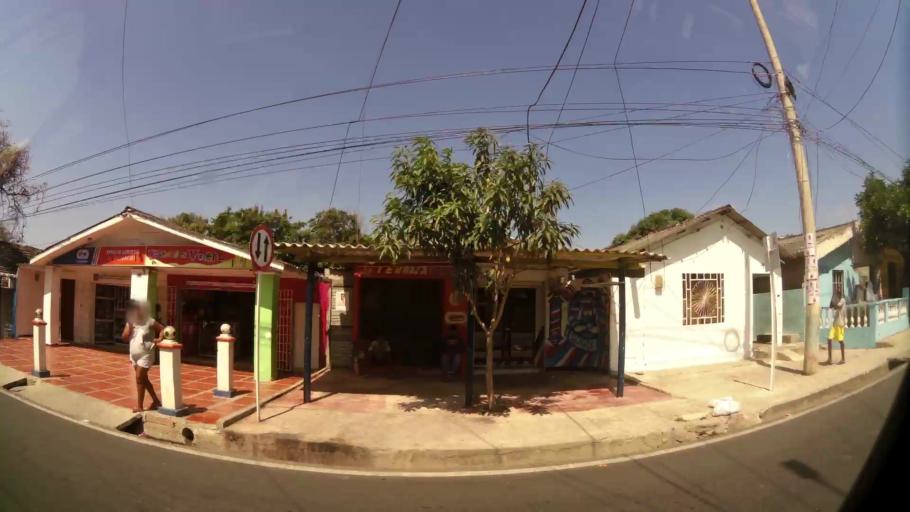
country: CO
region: Atlantico
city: Barranquilla
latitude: 10.9708
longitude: -74.8233
